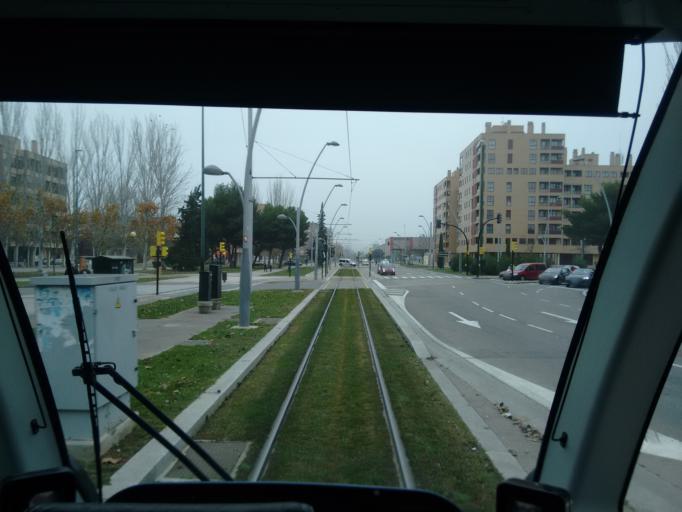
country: ES
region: Aragon
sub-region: Provincia de Zaragoza
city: Almozara
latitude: 41.6744
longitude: -0.8908
